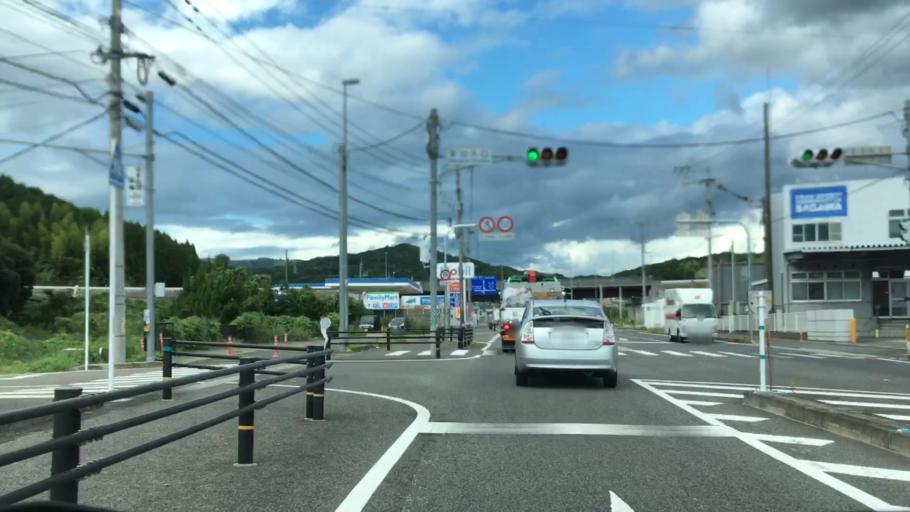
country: JP
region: Saga Prefecture
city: Imaricho-ko
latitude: 33.2802
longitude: 129.8956
